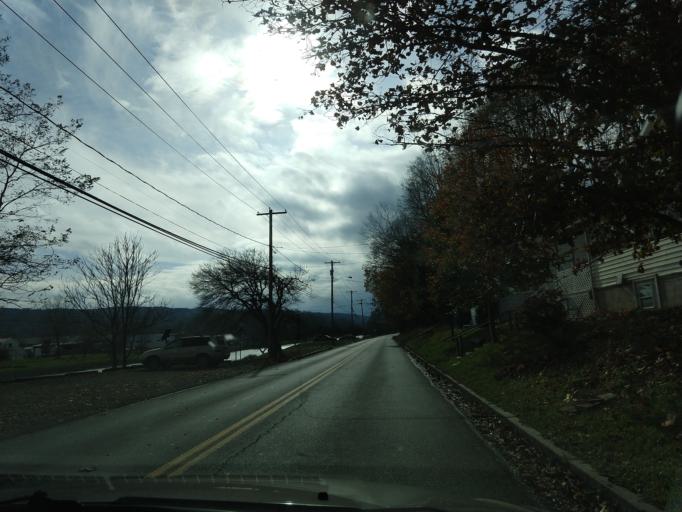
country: US
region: New York
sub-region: Tompkins County
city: Ithaca
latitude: 42.4377
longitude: -76.5175
